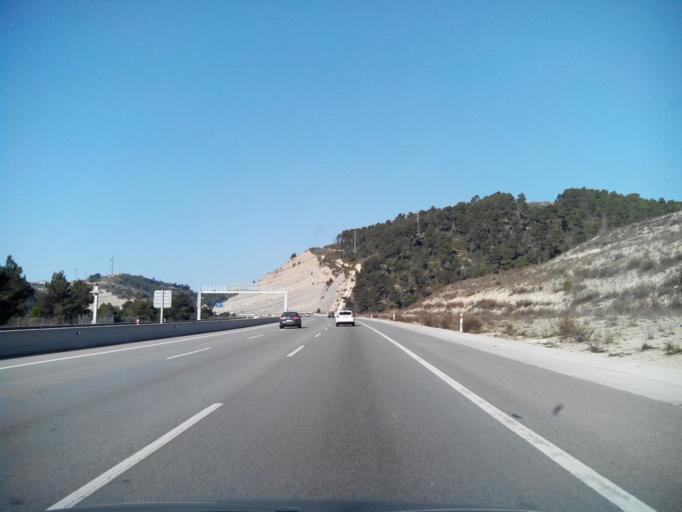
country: ES
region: Catalonia
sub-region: Provincia de Lleida
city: Sant Guim de Freixenet
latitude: 41.6238
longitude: 1.4354
